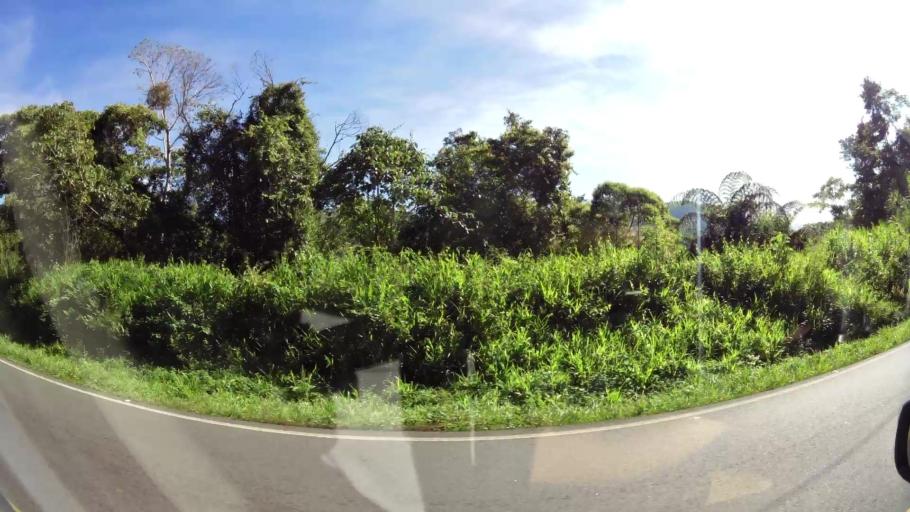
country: CR
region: San Jose
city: San Isidro
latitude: 9.4411
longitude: -83.7124
